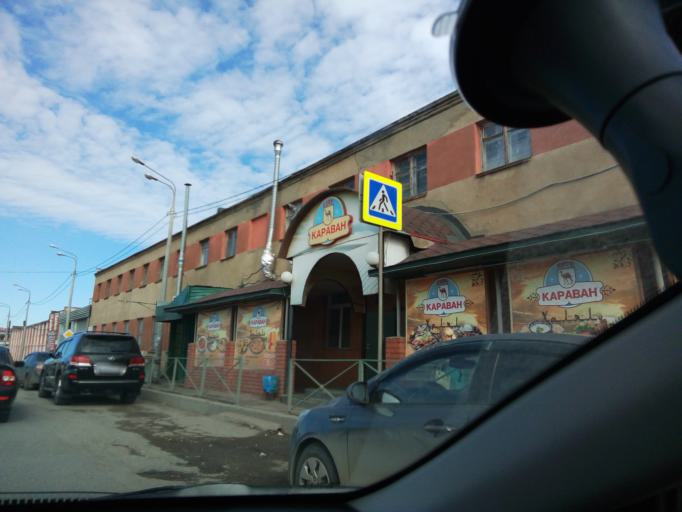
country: RU
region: Chuvashia
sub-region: Cheboksarskiy Rayon
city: Cheboksary
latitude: 56.1033
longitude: 47.2506
